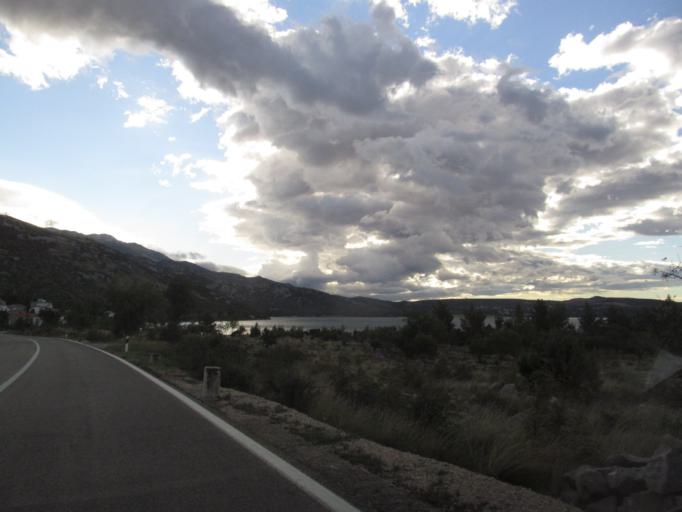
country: HR
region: Zadarska
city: Posedarje
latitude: 44.2737
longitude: 15.5013
